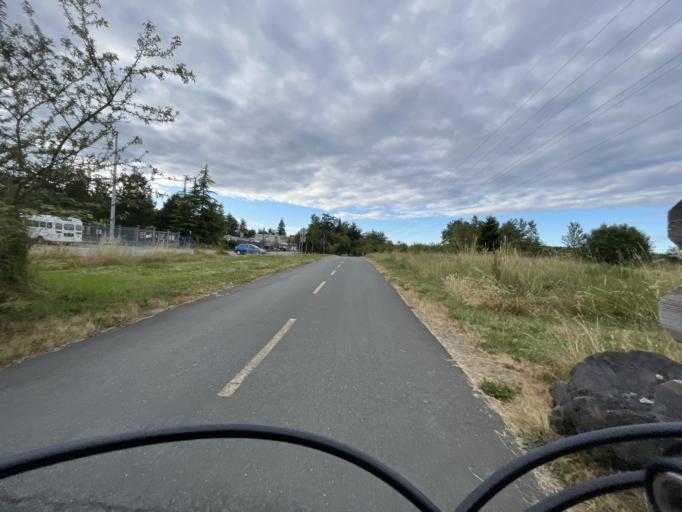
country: CA
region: British Columbia
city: Victoria
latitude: 48.4739
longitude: -123.3594
